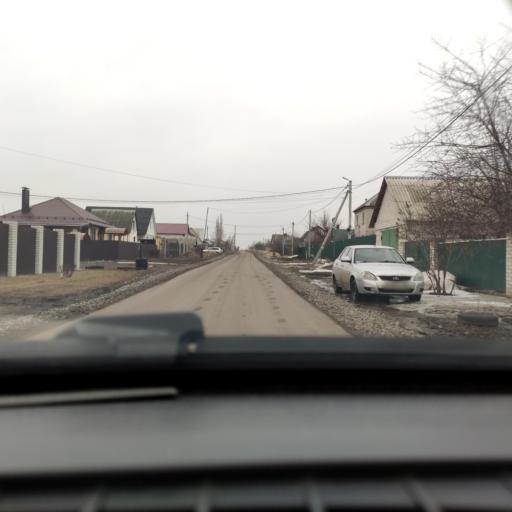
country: RU
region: Voronezj
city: Novaya Usman'
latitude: 51.6556
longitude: 39.4084
